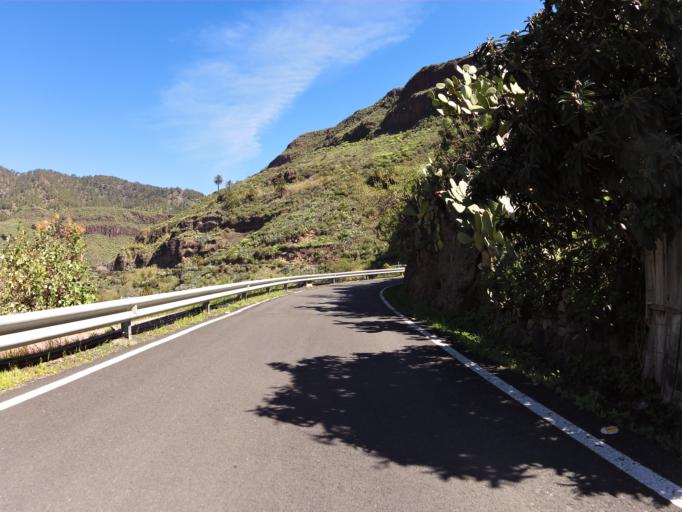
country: ES
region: Canary Islands
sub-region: Provincia de Las Palmas
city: Artenara
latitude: 28.0056
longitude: -15.6906
